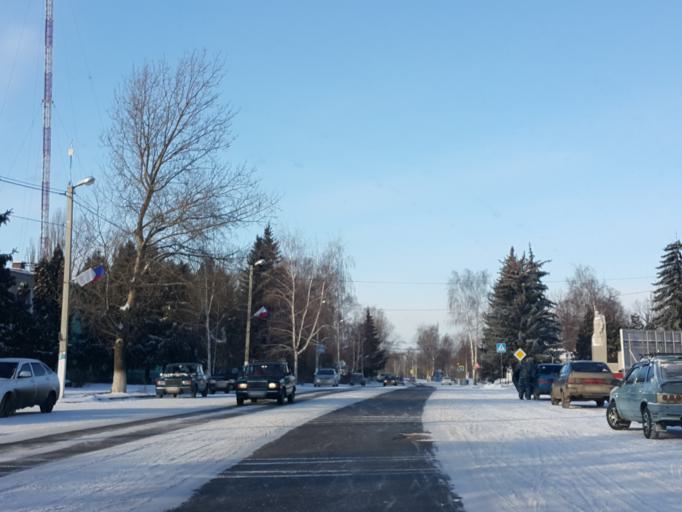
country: RU
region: Tambov
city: Znamenka
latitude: 52.4153
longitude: 41.4415
